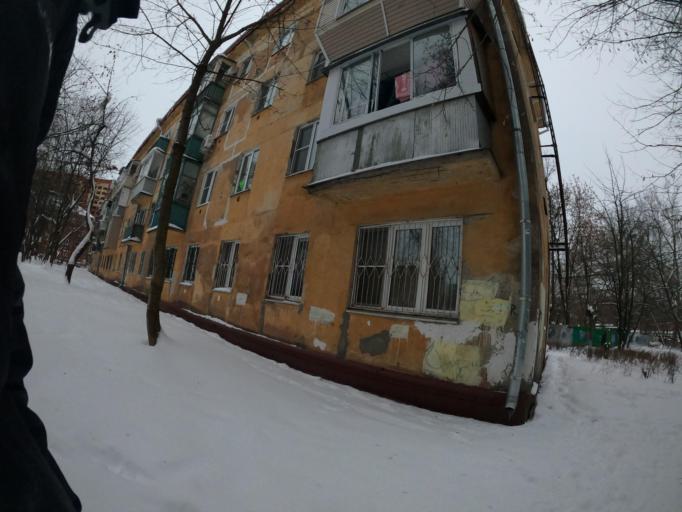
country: RU
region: Moskovskaya
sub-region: Podol'skiy Rayon
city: Podol'sk
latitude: 55.4148
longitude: 37.5374
